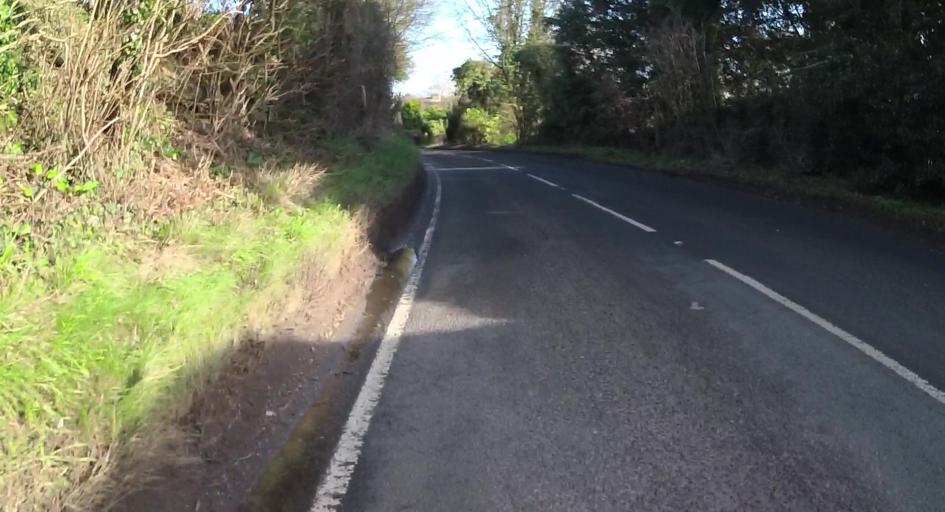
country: GB
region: England
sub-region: Hampshire
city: Kings Worthy
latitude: 51.0883
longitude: -1.2082
